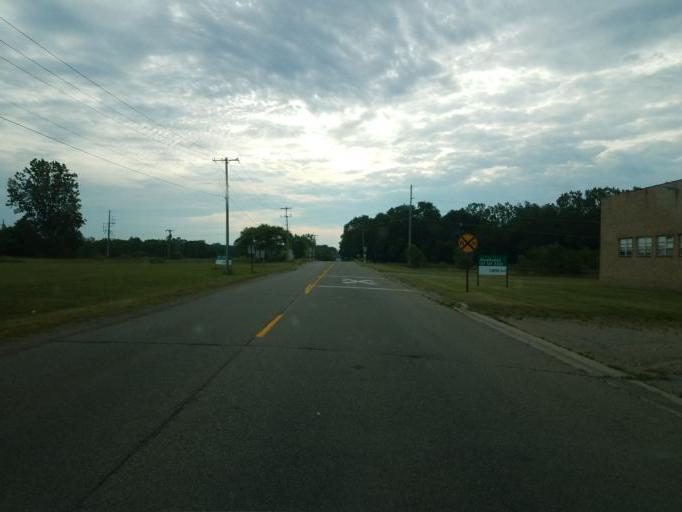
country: US
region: Michigan
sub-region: Eaton County
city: Charlotte
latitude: 42.5822
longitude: -84.8261
